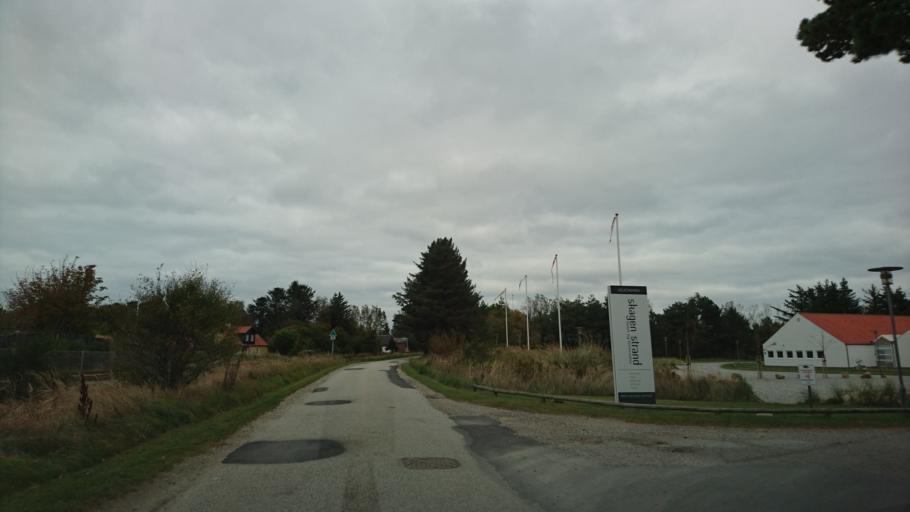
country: DK
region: North Denmark
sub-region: Frederikshavn Kommune
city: Skagen
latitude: 57.6601
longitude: 10.4640
